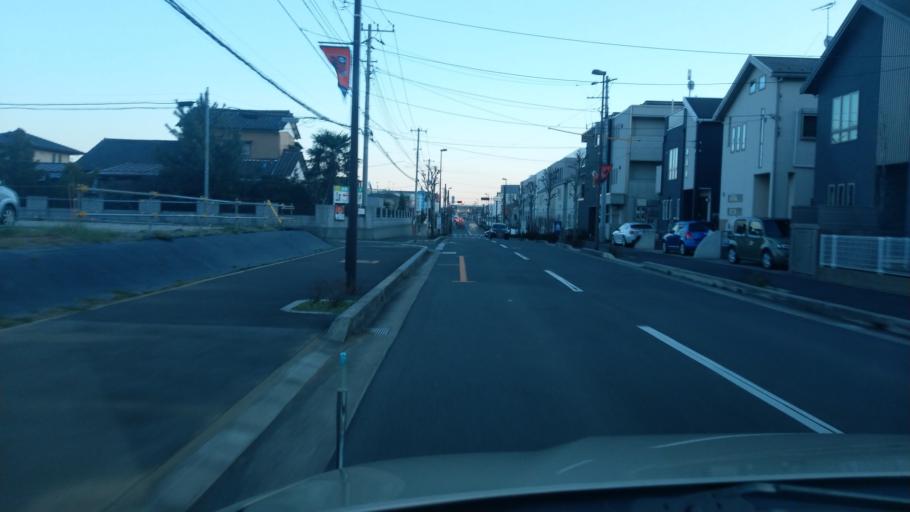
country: JP
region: Saitama
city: Ageoshimo
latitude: 35.9281
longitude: 139.5799
